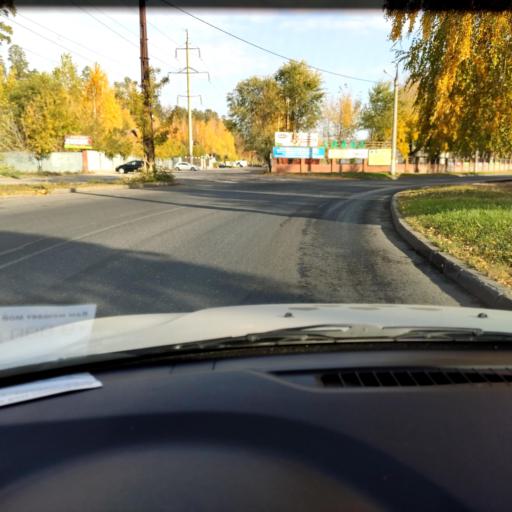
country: RU
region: Samara
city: Tol'yatti
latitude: 53.5077
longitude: 49.3912
